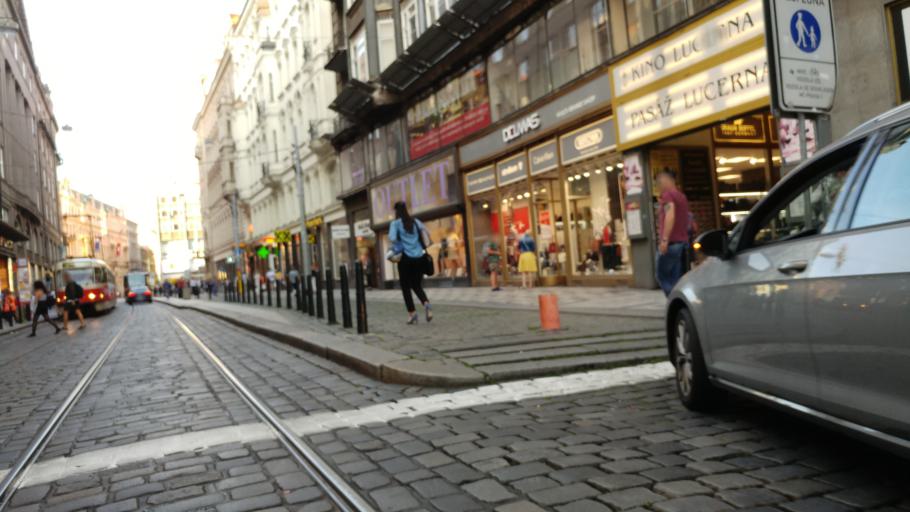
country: CZ
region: Praha
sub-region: Praha 1
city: Stare Mesto
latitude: 50.0814
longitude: 14.4250
